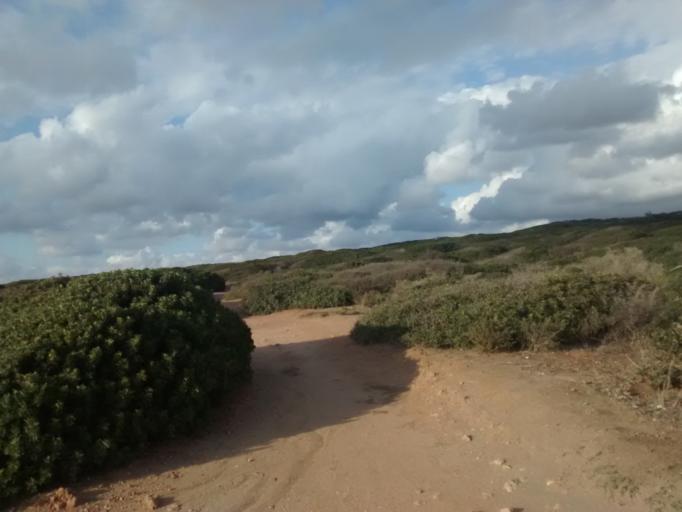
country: IT
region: Sardinia
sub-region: Provincia di Oristano
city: Narbolia
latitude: 40.0948
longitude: 8.4896
